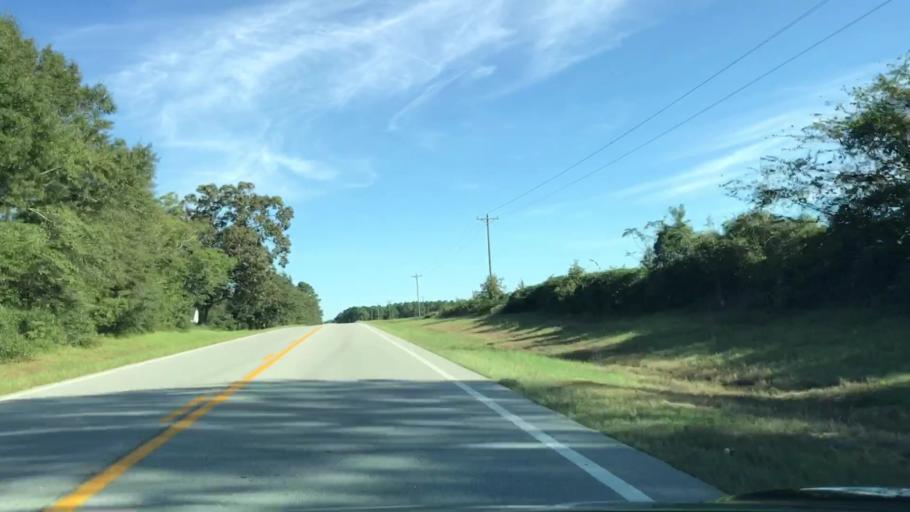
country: US
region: Georgia
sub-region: Glascock County
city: Gibson
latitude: 33.3144
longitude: -82.5432
